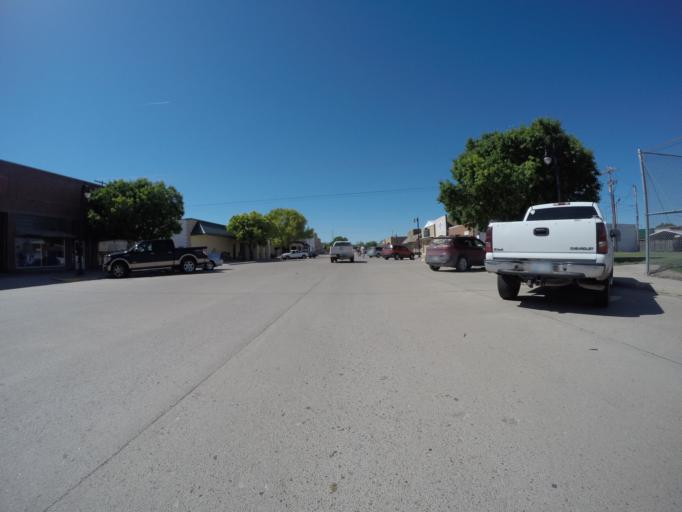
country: US
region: Kansas
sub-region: Rawlins County
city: Atwood
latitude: 39.8083
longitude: -101.0422
